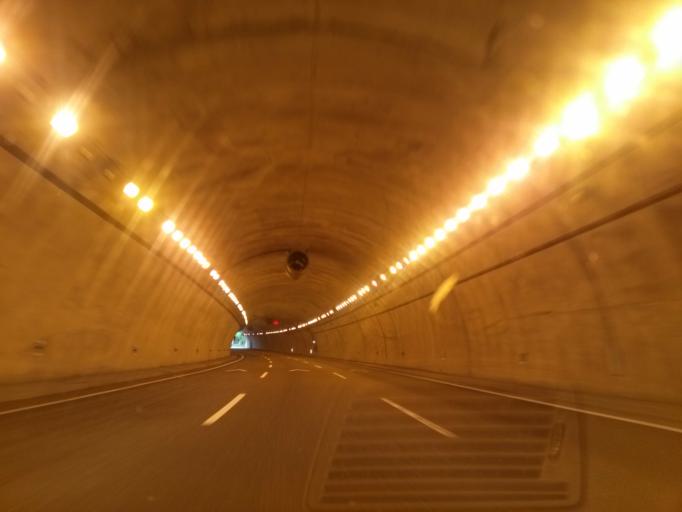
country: ES
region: Castille and Leon
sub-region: Provincia de Leon
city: Balboa
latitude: 42.7355
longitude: -7.0467
